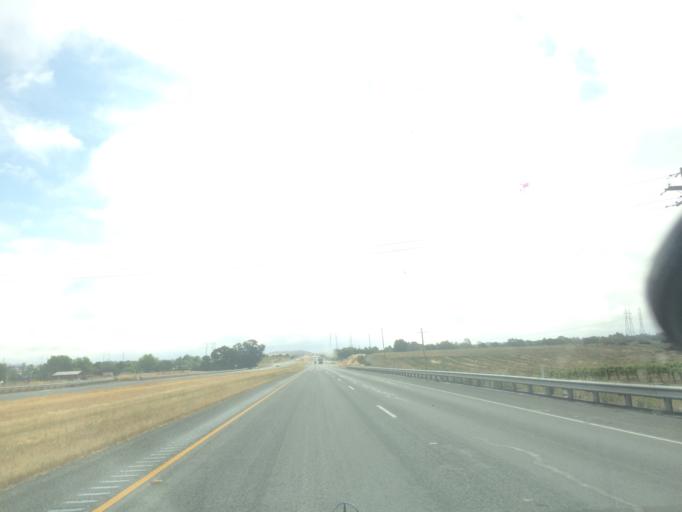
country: US
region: California
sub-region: San Luis Obispo County
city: Paso Robles
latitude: 35.6592
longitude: -120.5849
